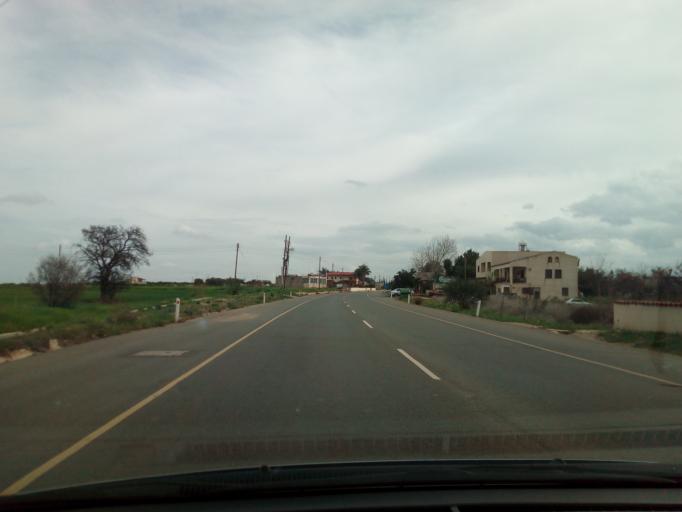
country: CY
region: Lefkosia
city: Peristerona
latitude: 35.1353
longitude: 33.0596
